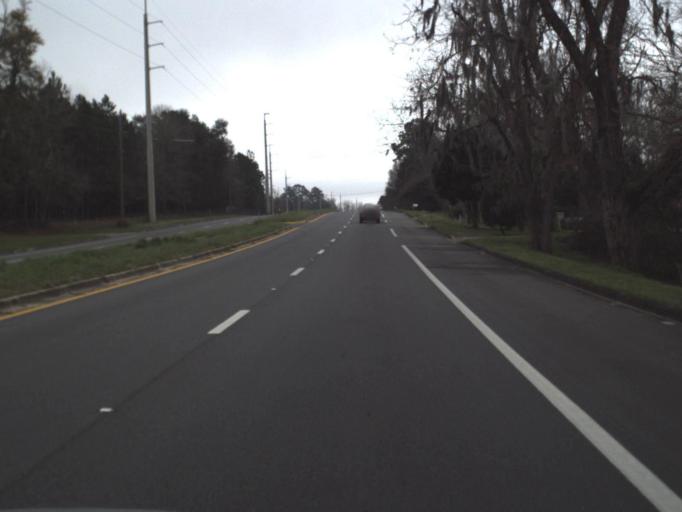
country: US
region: Florida
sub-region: Jefferson County
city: Monticello
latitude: 30.4116
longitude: -83.9525
